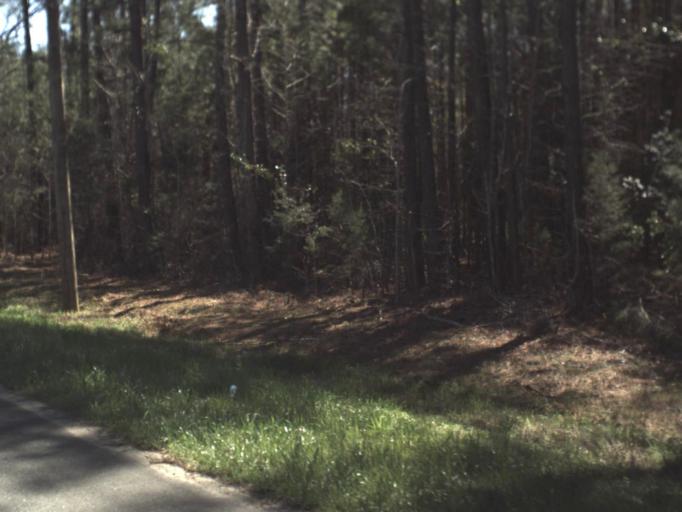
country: US
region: Florida
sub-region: Jackson County
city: Marianna
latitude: 30.8021
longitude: -85.2785
